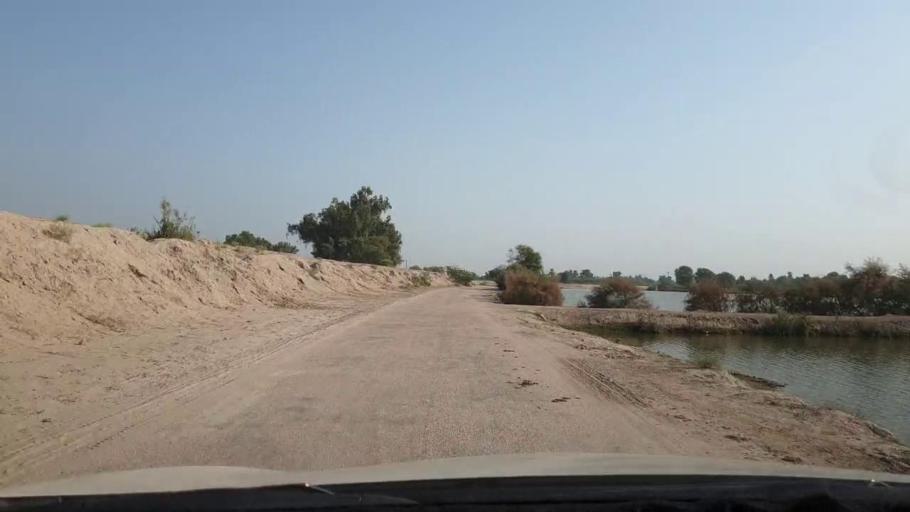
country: PK
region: Sindh
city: Larkana
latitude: 27.5482
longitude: 68.2558
